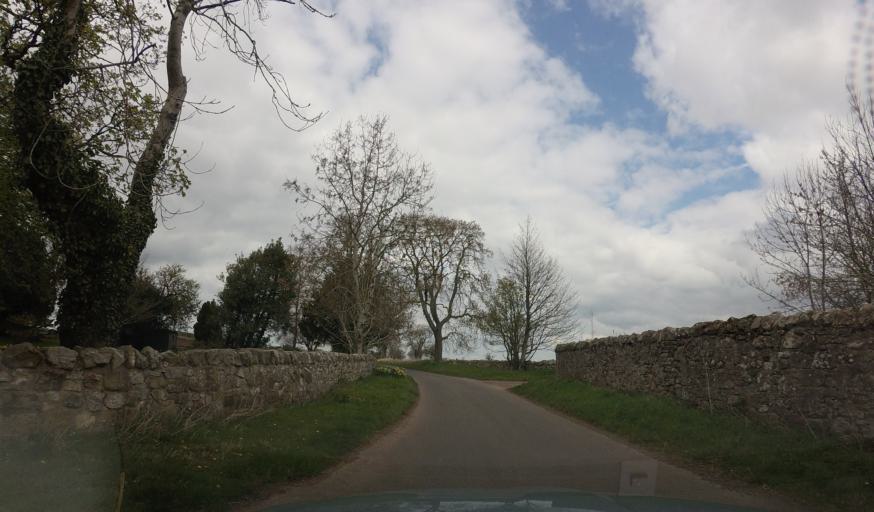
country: GB
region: Scotland
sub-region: Midlothian
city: Gorebridge
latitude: 55.8366
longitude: -3.0074
